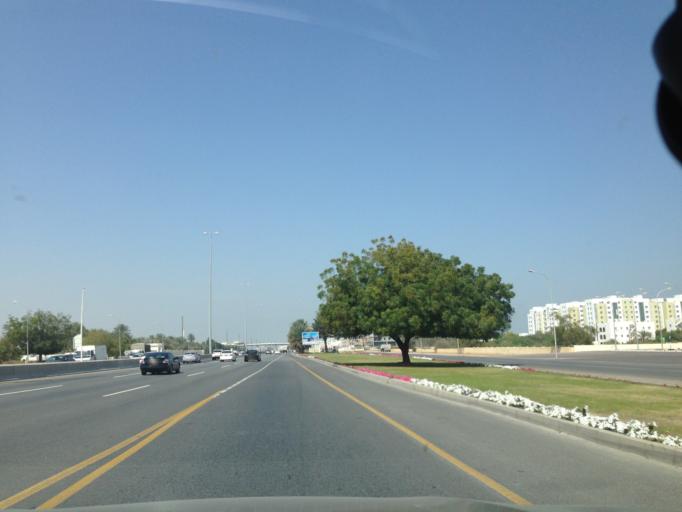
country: OM
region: Muhafazat Masqat
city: As Sib al Jadidah
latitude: 23.6177
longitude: 58.2424
